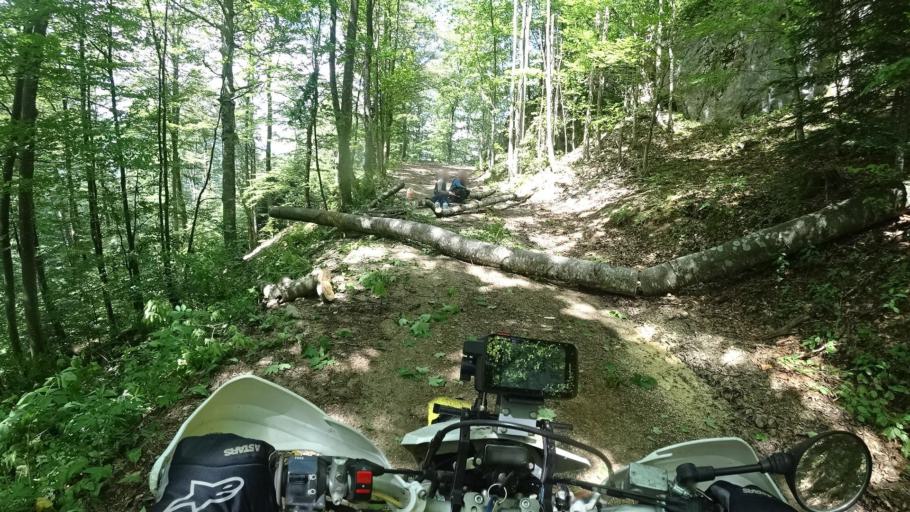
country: BA
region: Federation of Bosnia and Herzegovina
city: Orasac
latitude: 44.7363
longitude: 16.1555
